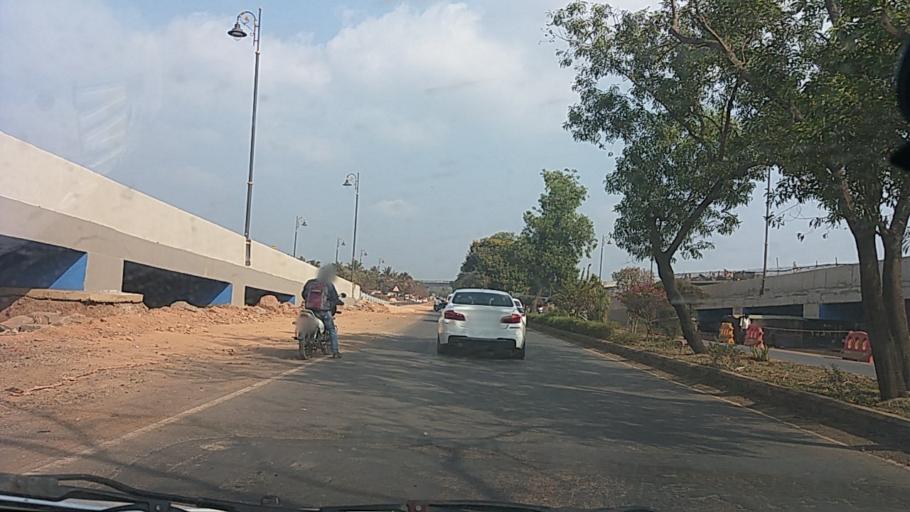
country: IN
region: Goa
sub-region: North Goa
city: Panaji
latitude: 15.4935
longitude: 73.8408
